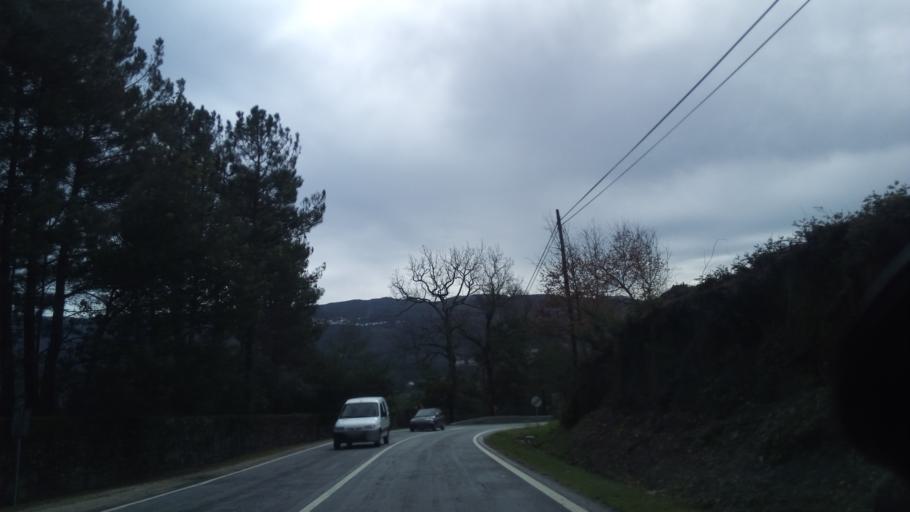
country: PT
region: Guarda
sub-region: Seia
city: Seia
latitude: 40.4419
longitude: -7.7097
